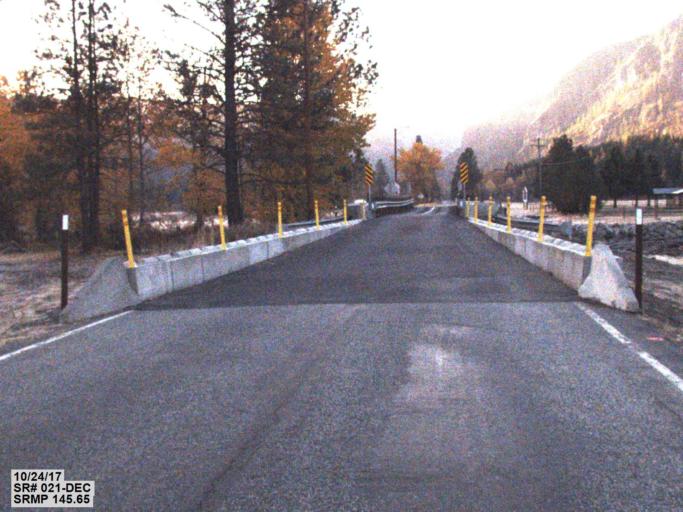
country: US
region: Washington
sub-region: Ferry County
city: Republic
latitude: 48.4592
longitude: -118.7506
